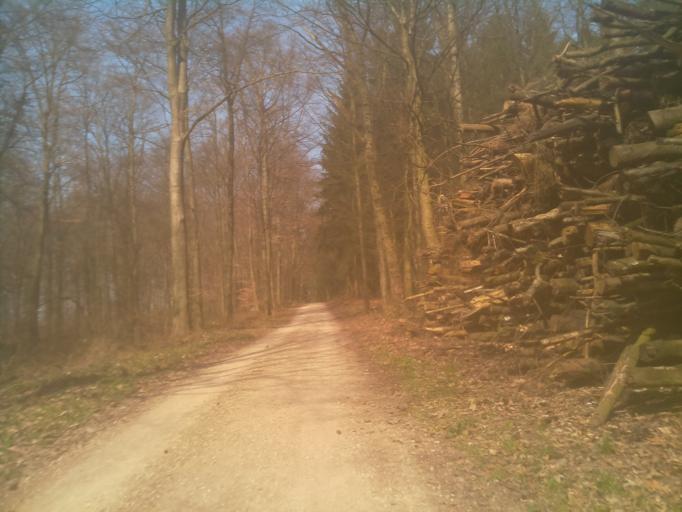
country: DE
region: Hesse
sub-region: Regierungsbezirk Darmstadt
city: Birkenau
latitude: 49.5786
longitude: 8.6838
